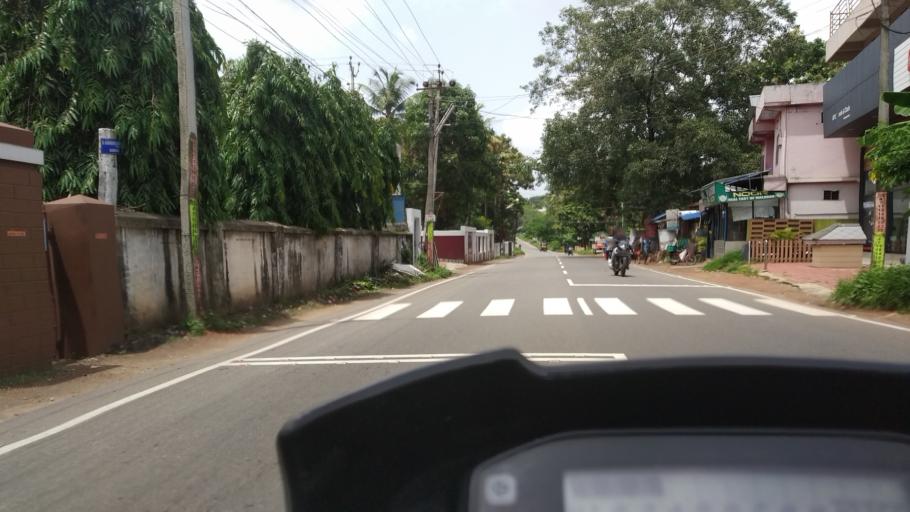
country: IN
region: Kerala
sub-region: Ernakulam
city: Aluva
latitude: 10.1264
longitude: 76.3210
